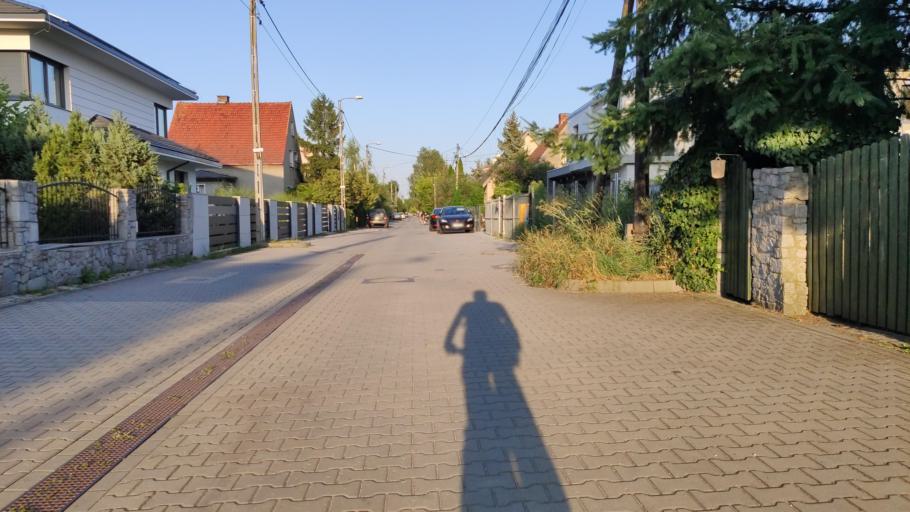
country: PL
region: Lower Silesian Voivodeship
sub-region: Powiat wroclawski
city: Zerniki Wroclawskie
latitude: 51.0576
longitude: 17.0611
